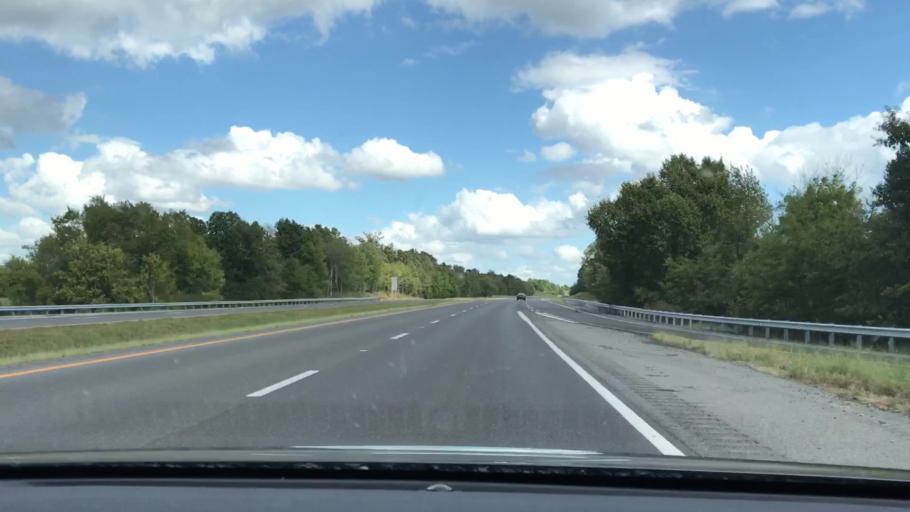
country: US
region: Kentucky
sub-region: Graves County
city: Mayfield
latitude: 36.7763
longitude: -88.5931
